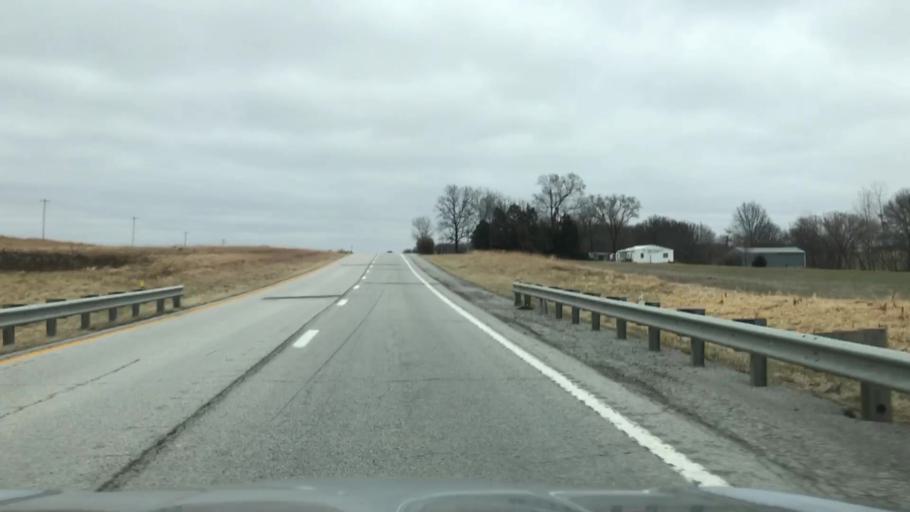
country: US
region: Missouri
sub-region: Linn County
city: Linneus
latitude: 39.7776
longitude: -93.2750
